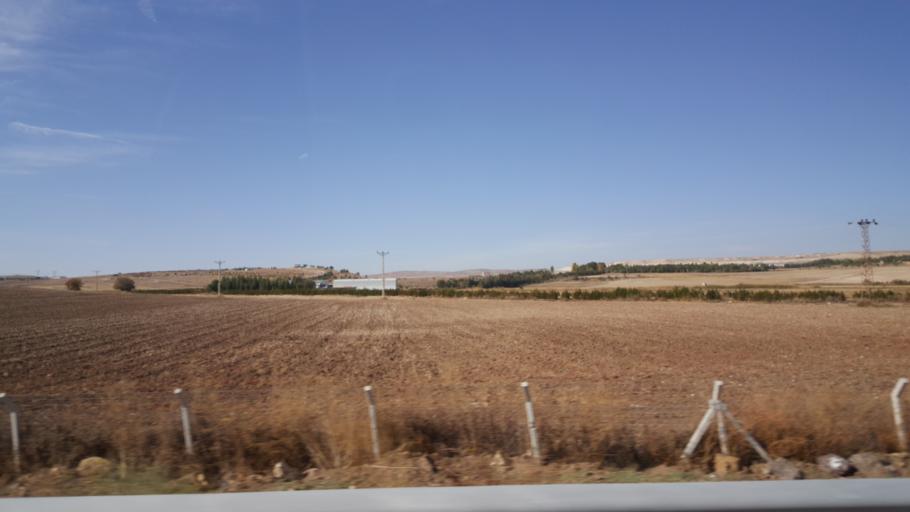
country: TR
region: Ankara
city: Ikizce
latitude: 39.6078
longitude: 32.6786
